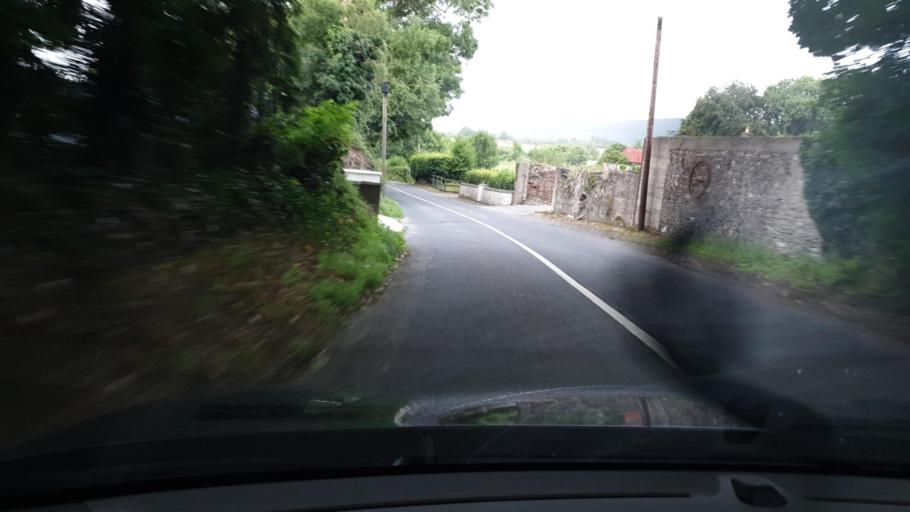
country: IE
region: Leinster
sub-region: South Dublin
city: Rathcoole
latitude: 53.2385
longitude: -6.5169
